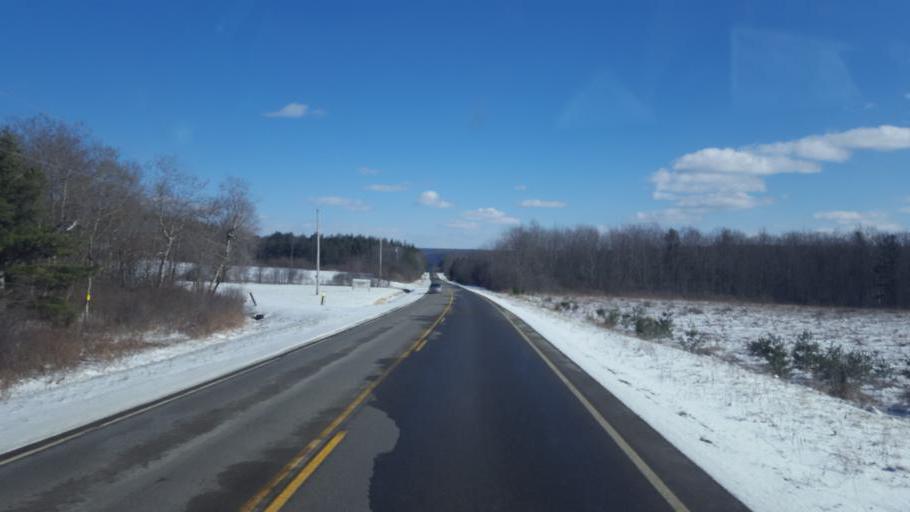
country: US
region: New York
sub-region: Allegany County
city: Friendship
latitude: 42.1845
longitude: -78.0848
